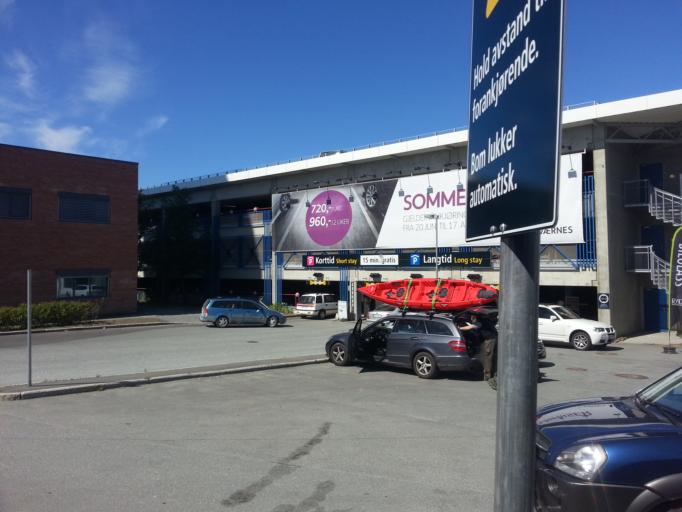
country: NO
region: Nord-Trondelag
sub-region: Stjordal
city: Stjordal
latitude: 63.4529
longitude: 10.9186
